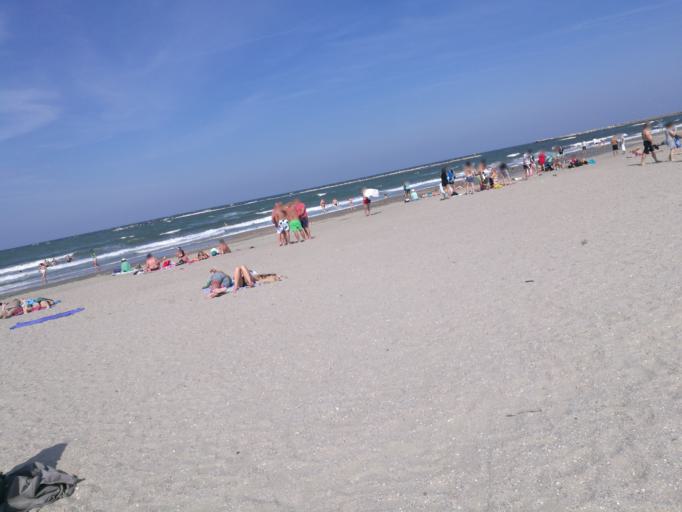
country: RO
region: Constanta
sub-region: Municipiul Constanta
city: Palazu Mare
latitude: 44.2224
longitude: 28.6343
